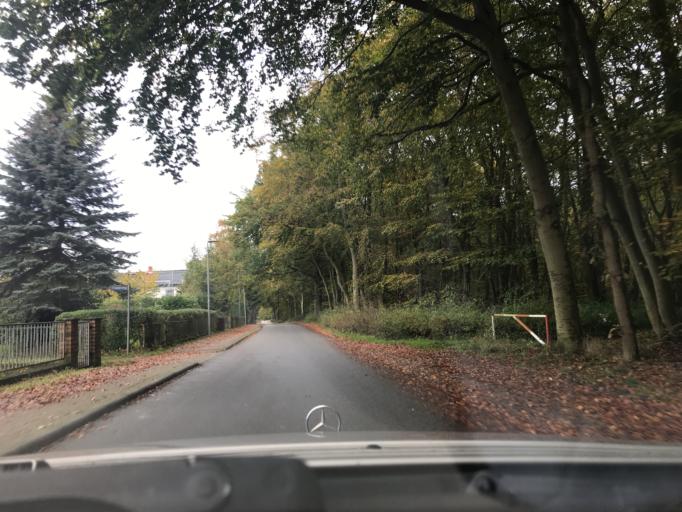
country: DE
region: Mecklenburg-Vorpommern
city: Loddin
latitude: 54.0288
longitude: 14.0338
